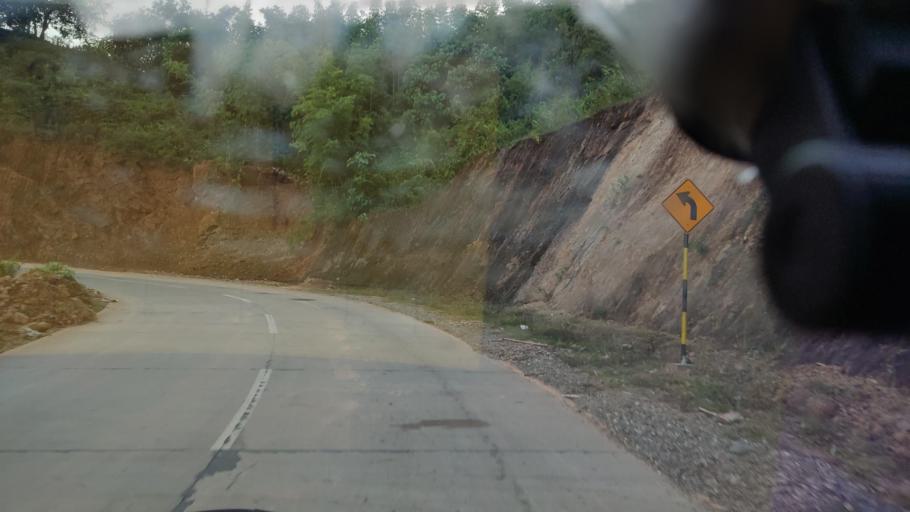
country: MM
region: Magway
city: Minbu
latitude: 19.8254
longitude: 94.0747
